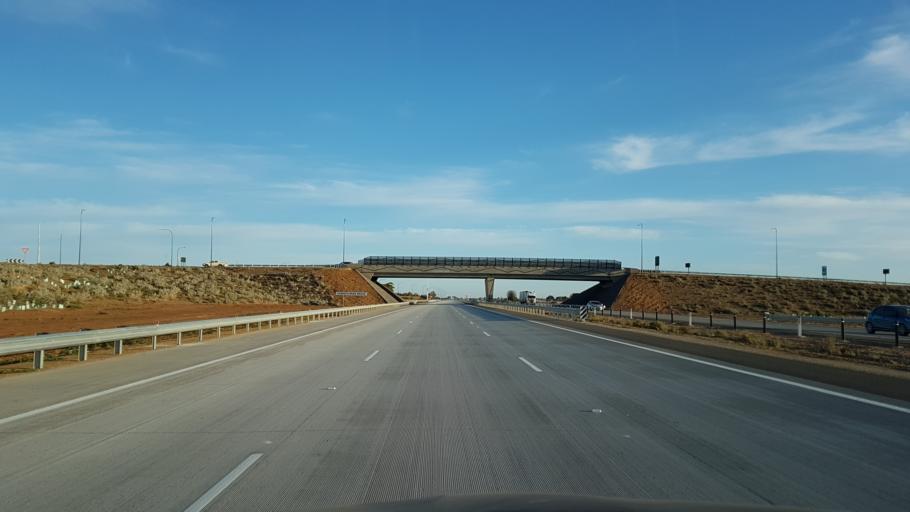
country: AU
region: South Australia
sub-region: Salisbury
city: Salisbury
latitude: -34.7344
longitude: 138.5771
